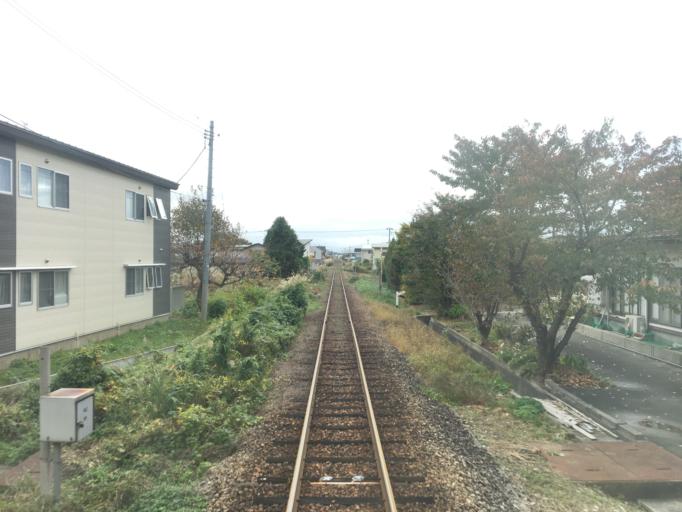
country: JP
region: Yamagata
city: Nagai
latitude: 38.1025
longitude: 140.0340
